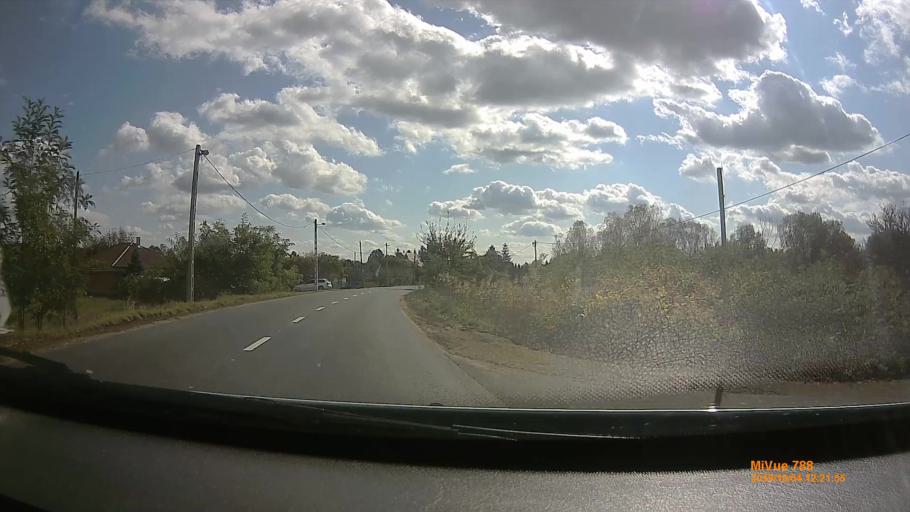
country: HU
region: Szabolcs-Szatmar-Bereg
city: Kotaj
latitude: 48.0164
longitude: 21.6863
